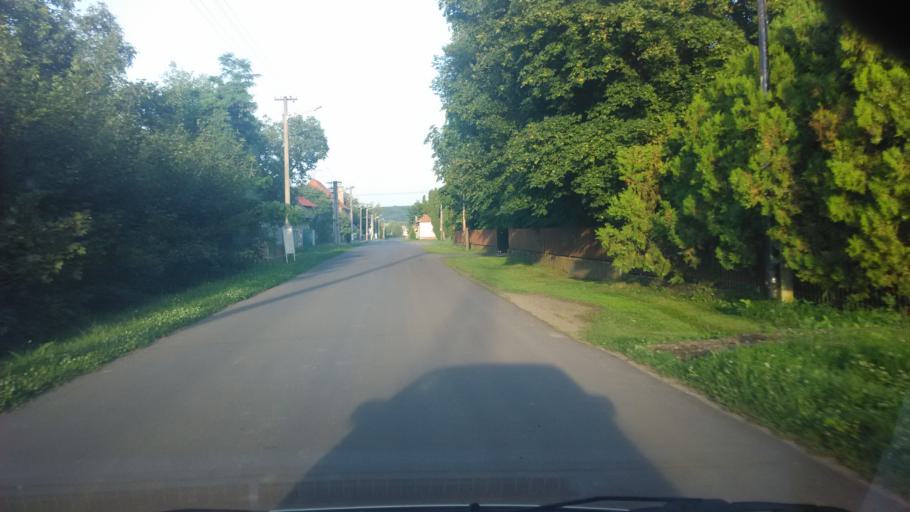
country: SK
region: Nitriansky
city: Zeliezovce
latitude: 48.0196
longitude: 18.8018
